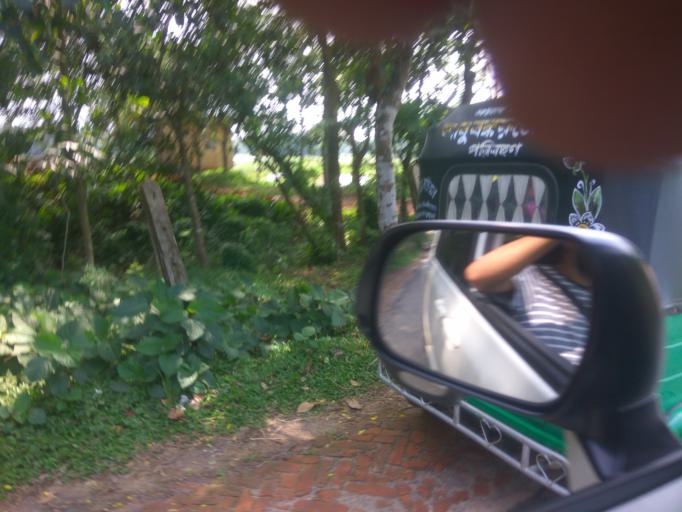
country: IN
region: Assam
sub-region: Karimganj
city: Karimganj
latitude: 24.8106
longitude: 92.1820
